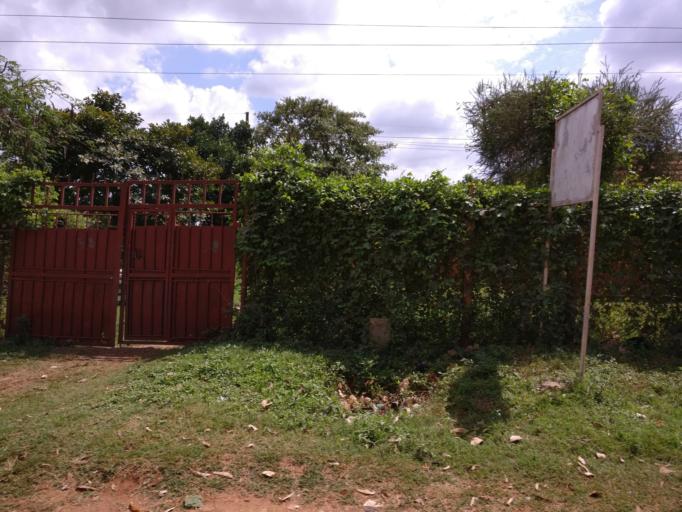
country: UG
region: Central Region
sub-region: Kampala District
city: Kampala
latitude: 0.2848
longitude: 32.5661
